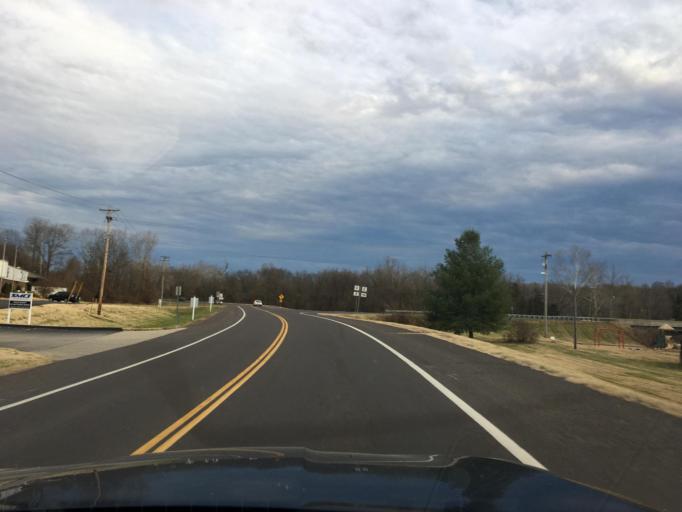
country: US
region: Missouri
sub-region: Jefferson County
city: De Soto
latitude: 38.1161
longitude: -90.5601
